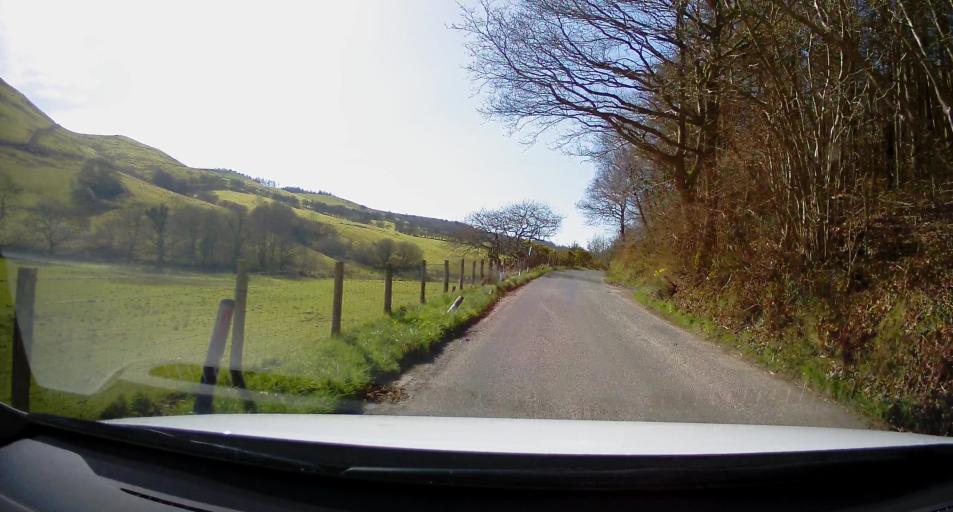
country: GB
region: Wales
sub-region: County of Ceredigion
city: Lledrod
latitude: 52.3550
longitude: -3.9222
